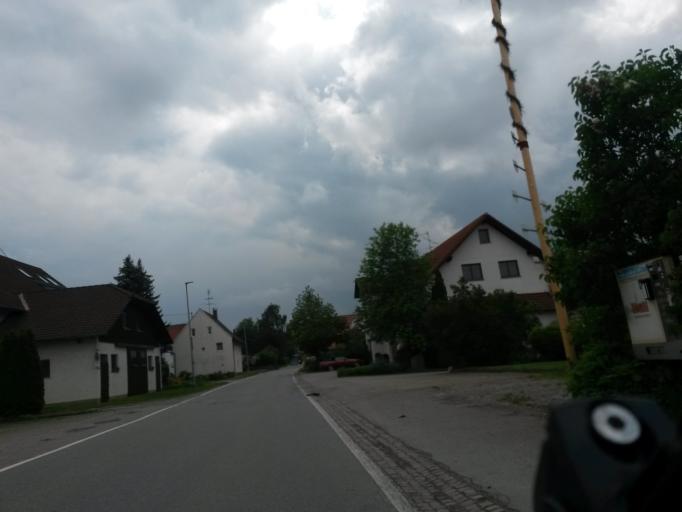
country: DE
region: Baden-Wuerttemberg
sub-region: Tuebingen Region
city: Bad Waldsee
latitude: 47.9354
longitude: 9.8154
